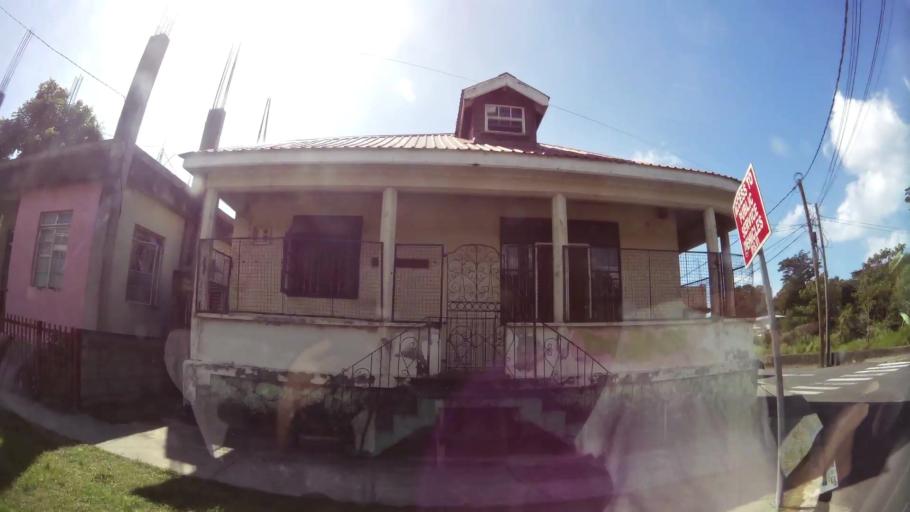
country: DM
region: Saint George
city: Roseau
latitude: 15.3021
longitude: -61.3862
